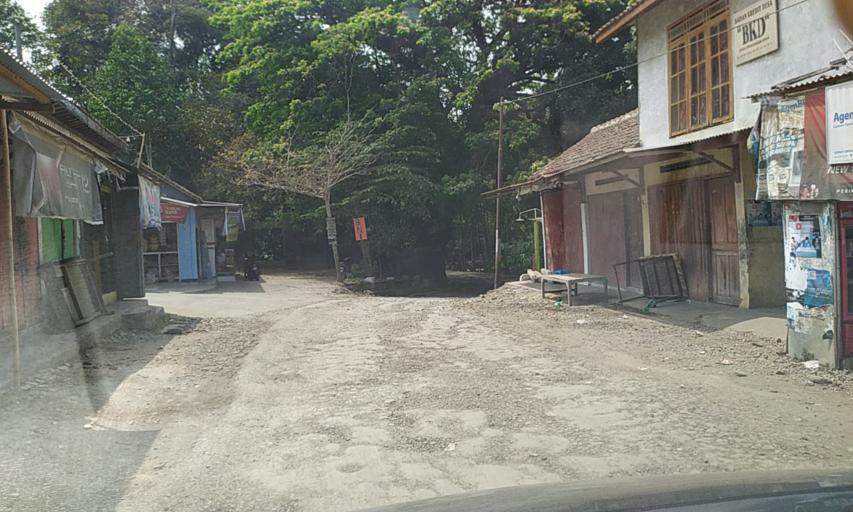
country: ID
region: Central Java
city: Watuagung
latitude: -7.5930
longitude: 109.1151
